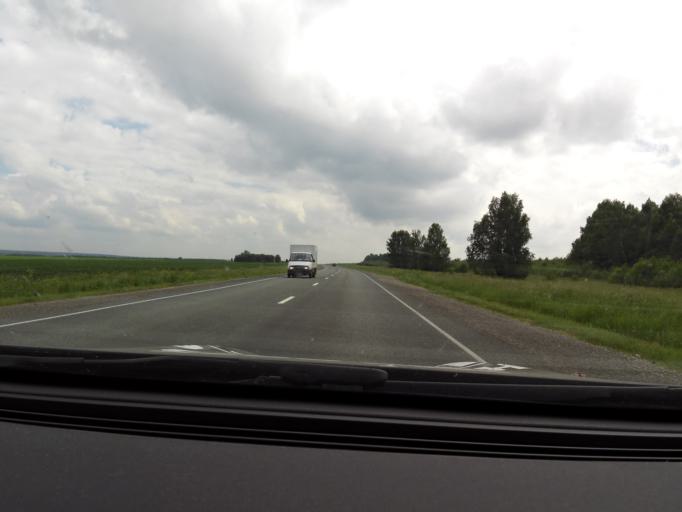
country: RU
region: Perm
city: Suksun
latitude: 56.9422
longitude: 57.5336
